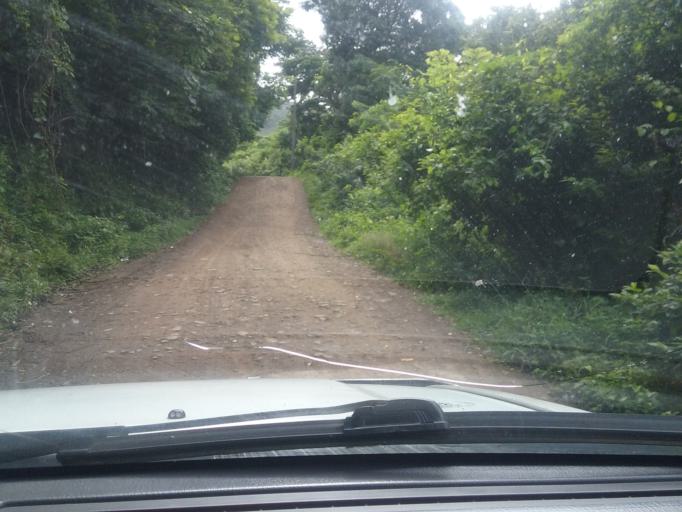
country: NI
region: Matagalpa
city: Matagalpa
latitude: 12.8718
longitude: -85.9424
